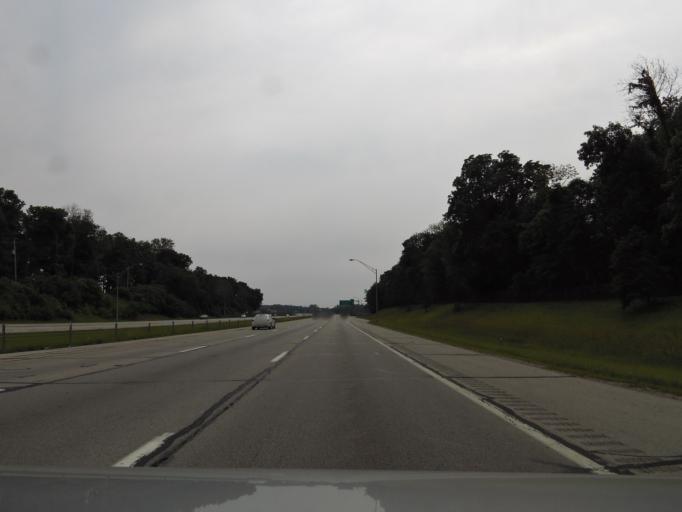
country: US
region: Ohio
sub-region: Montgomery County
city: Centerville
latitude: 39.6548
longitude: -84.1180
